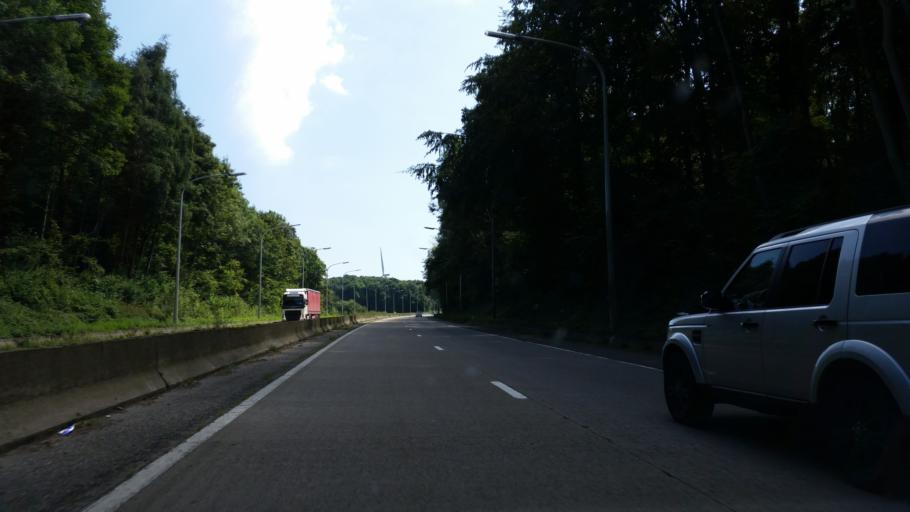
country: BE
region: Wallonia
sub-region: Province de Namur
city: Hamois
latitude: 50.3034
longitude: 5.1639
